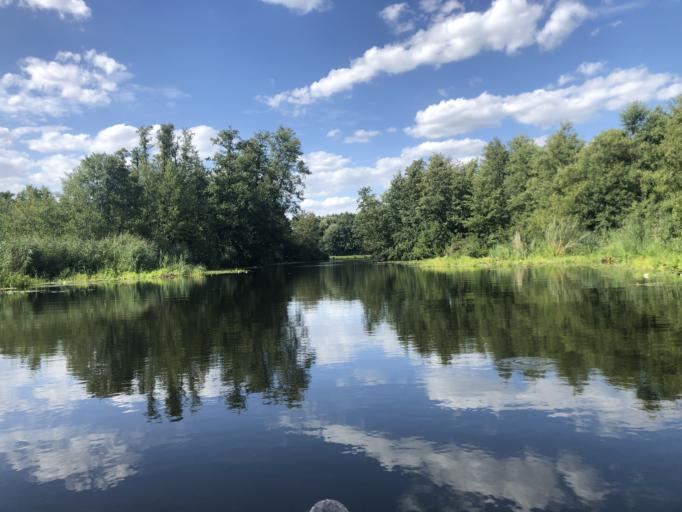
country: DE
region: Brandenburg
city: Mullrose
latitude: 52.2487
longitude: 14.4301
